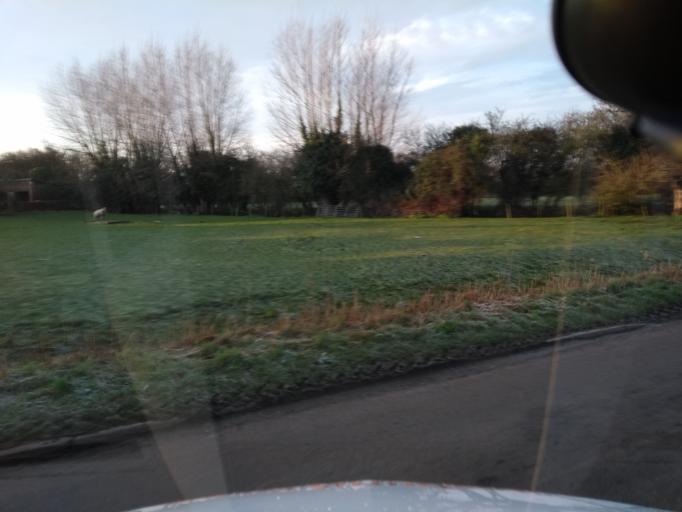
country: GB
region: England
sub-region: Somerset
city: Woolavington
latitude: 51.2185
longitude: -2.9282
